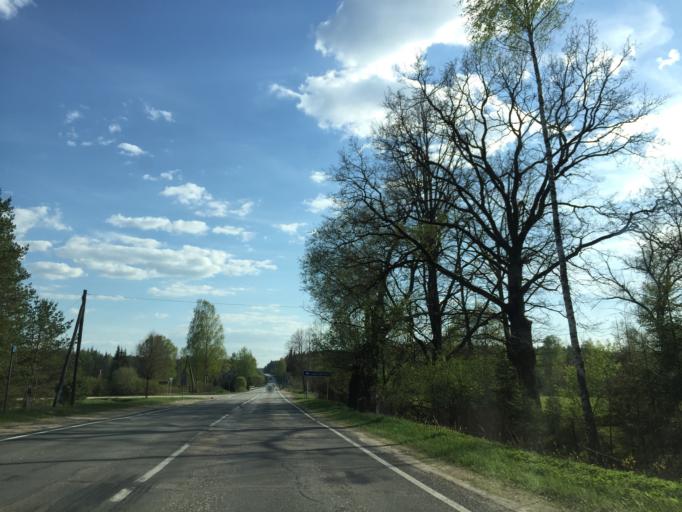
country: LV
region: Pargaujas
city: Stalbe
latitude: 57.2975
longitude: 24.9244
